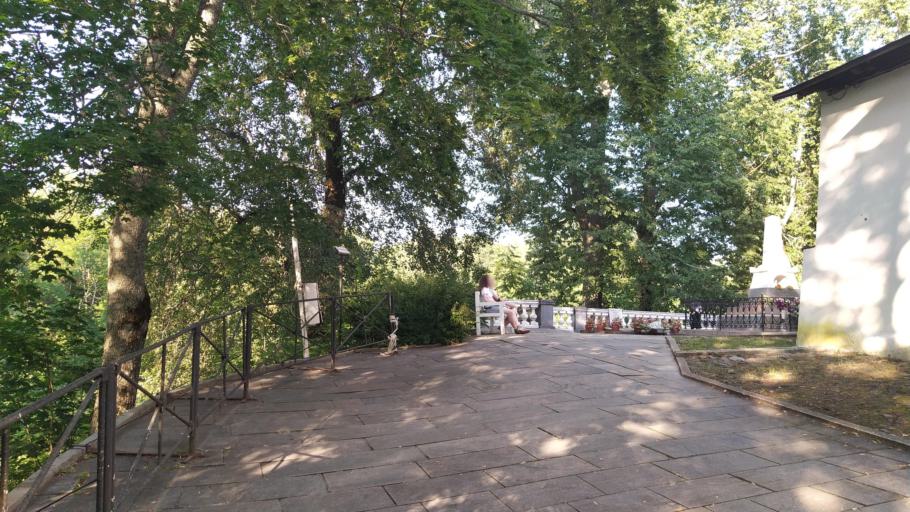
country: RU
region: Pskov
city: Pushkinskiye Gory
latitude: 57.0227
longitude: 28.9195
